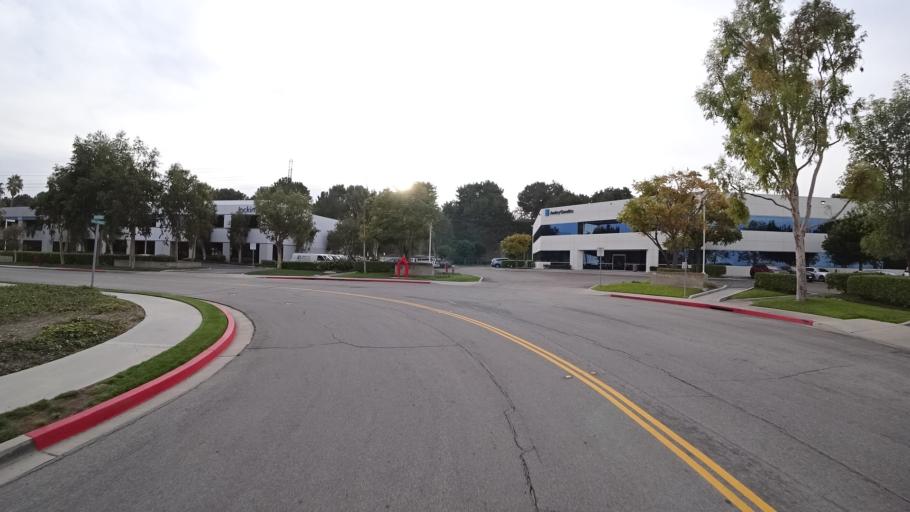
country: US
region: California
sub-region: Orange County
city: Laguna Woods
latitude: 33.5935
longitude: -117.7263
